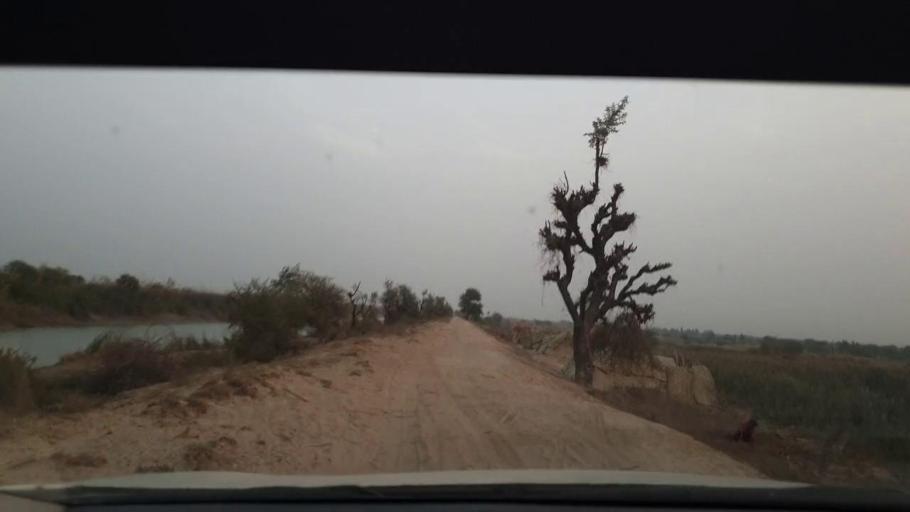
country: PK
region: Sindh
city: Berani
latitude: 25.8640
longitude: 68.7736
